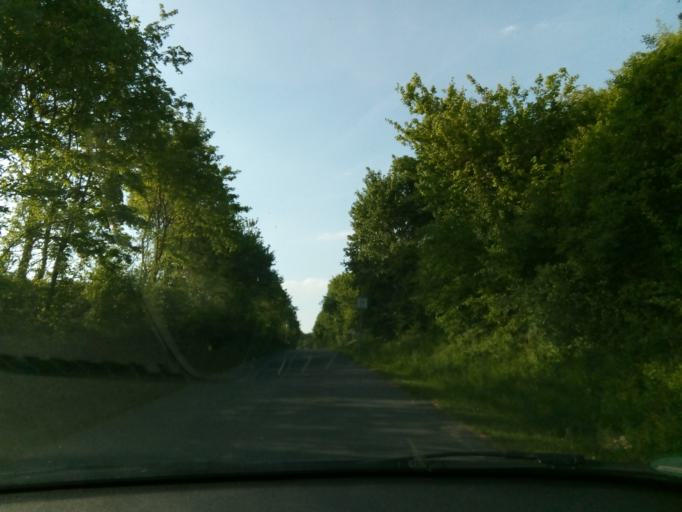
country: DE
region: Bavaria
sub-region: Regierungsbezirk Unterfranken
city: Oberschwarzach
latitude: 49.8615
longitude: 10.4134
